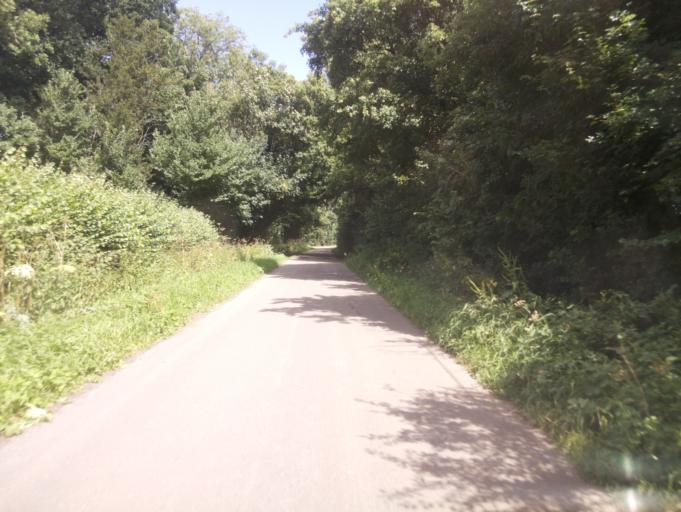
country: GB
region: England
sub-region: Wiltshire
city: Biddestone
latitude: 51.5147
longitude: -2.1971
